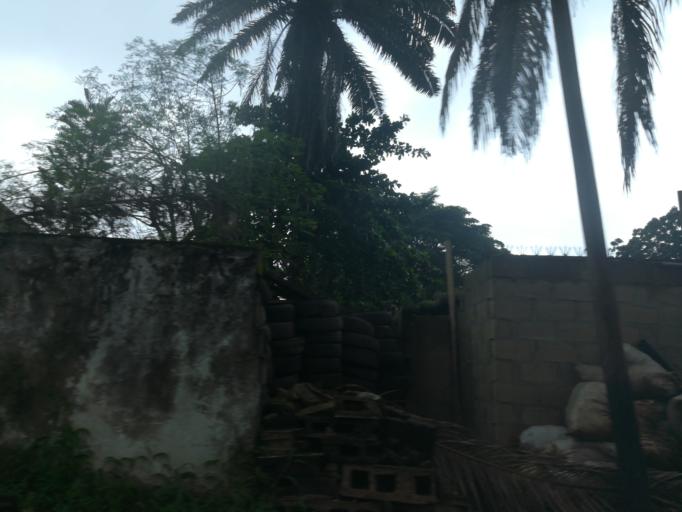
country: NG
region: Lagos
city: Ojota
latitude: 6.5677
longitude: 3.3688
